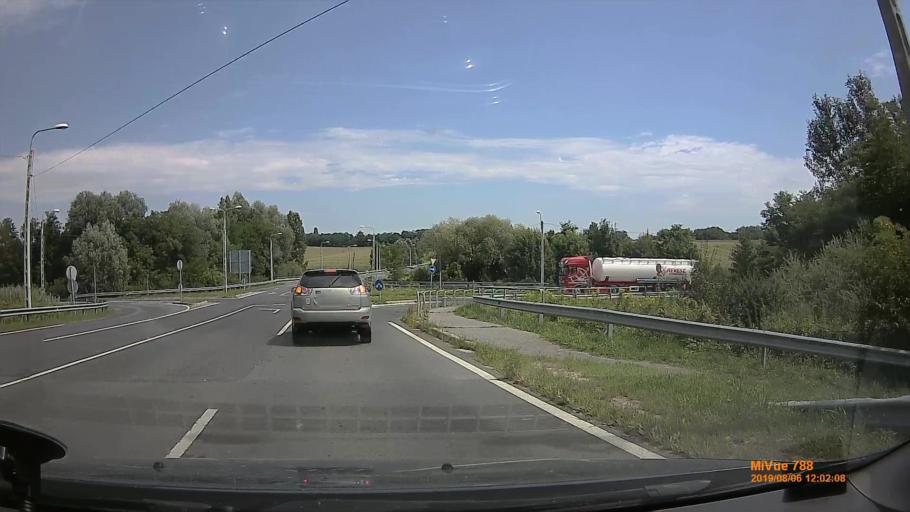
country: HU
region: Zala
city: Becsehely
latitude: 46.4520
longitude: 16.8119
